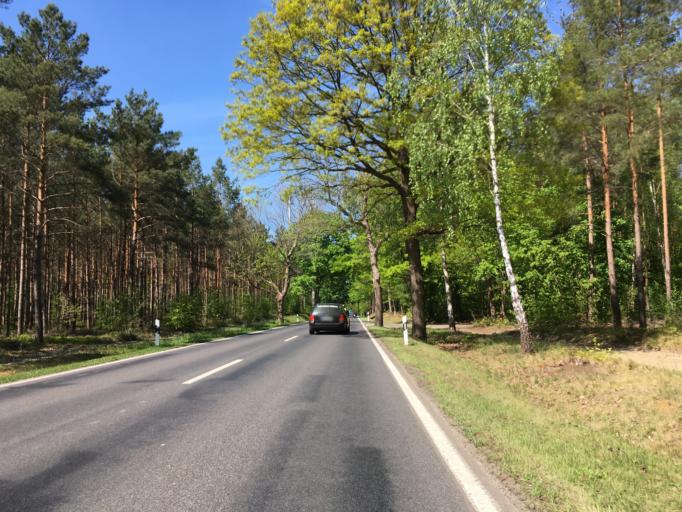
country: DE
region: Brandenburg
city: Marienwerder
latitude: 52.7789
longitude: 13.5586
